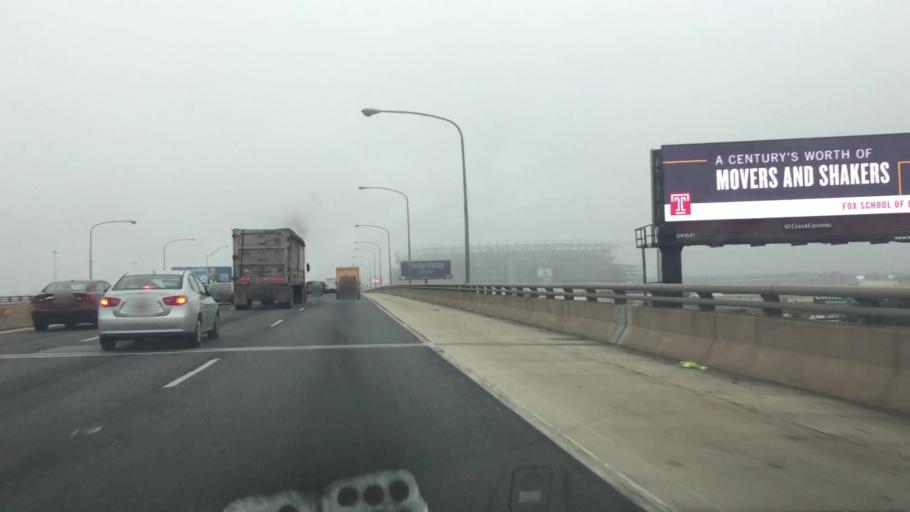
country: US
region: New Jersey
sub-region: Camden County
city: Gloucester City
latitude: 39.9008
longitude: -75.1559
